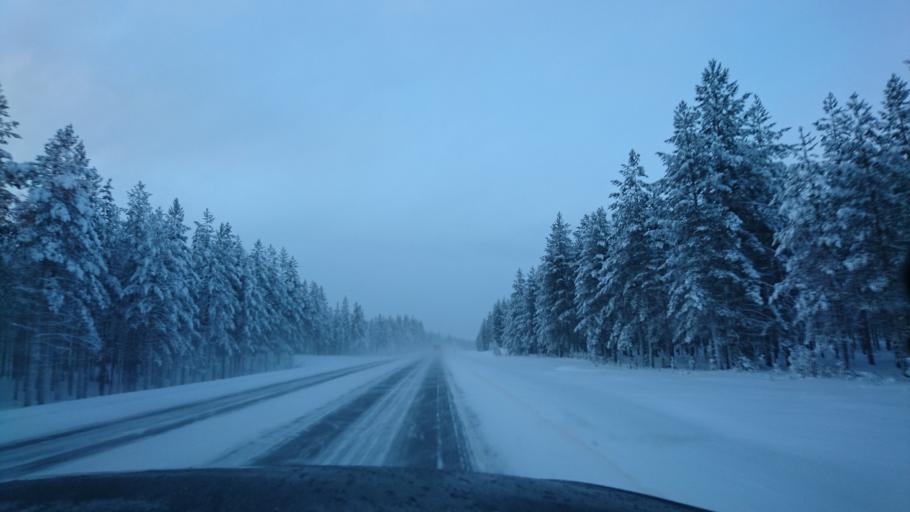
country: FI
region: Kainuu
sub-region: Kehys-Kainuu
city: Puolanka
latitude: 65.4329
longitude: 27.5770
